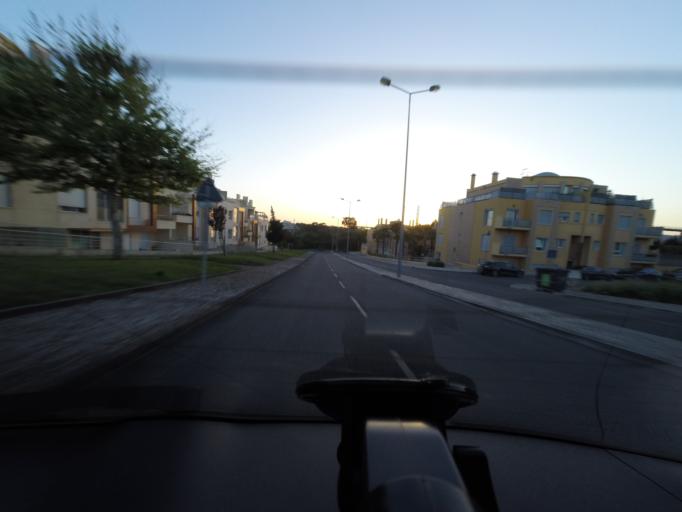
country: PT
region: Lisbon
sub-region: Cascais
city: Sao Domingos de Rana
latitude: 38.7071
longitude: -9.3295
